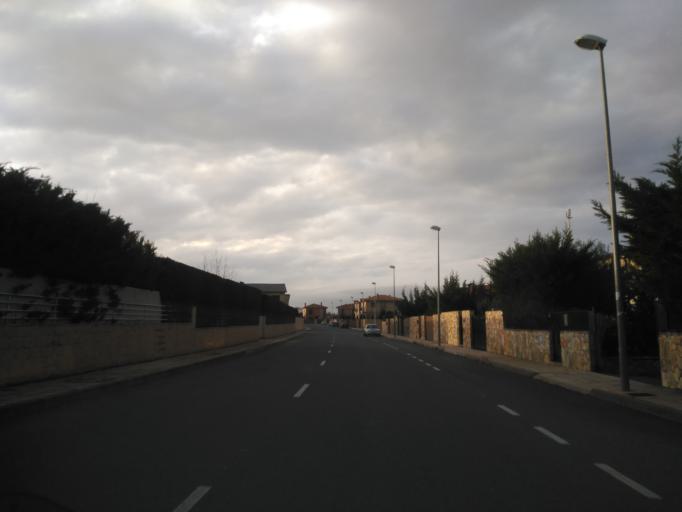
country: ES
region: Castille and Leon
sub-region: Provincia de Salamanca
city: Santa Marta de Tormes
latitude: 40.9315
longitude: -5.6257
